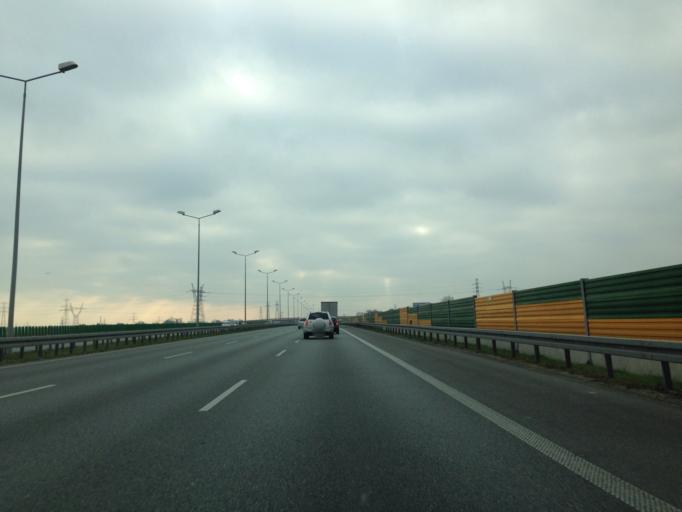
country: PL
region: Masovian Voivodeship
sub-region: Warszawa
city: Ursus
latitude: 52.2277
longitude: 20.8759
